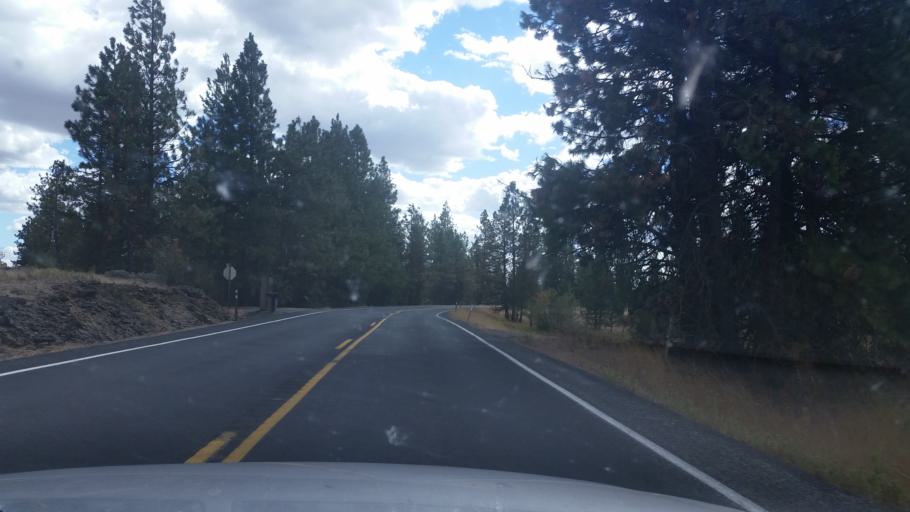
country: US
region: Washington
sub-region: Spokane County
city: Medical Lake
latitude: 47.5449
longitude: -117.7046
